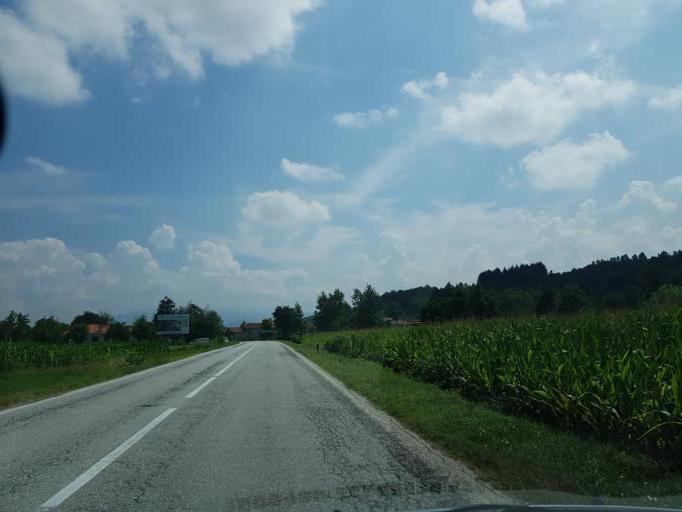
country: IT
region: Piedmont
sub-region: Provincia di Cuneo
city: Cervasca
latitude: 44.3879
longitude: 7.4616
